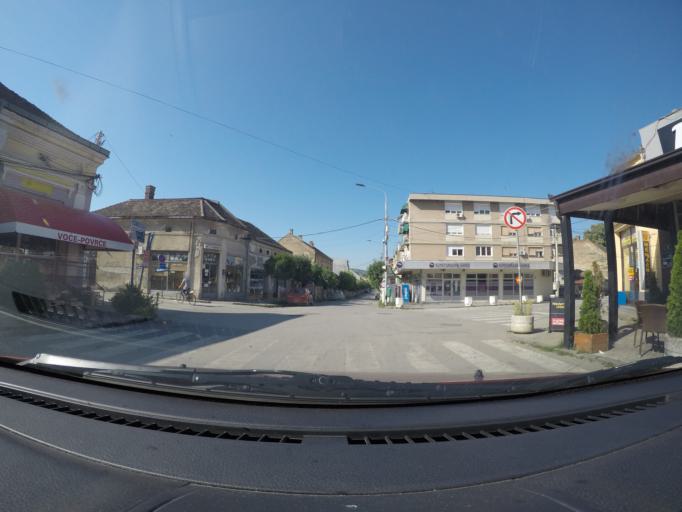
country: RS
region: Central Serbia
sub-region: Branicevski Okrug
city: Veliko Gradiste
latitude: 44.7632
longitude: 21.5164
